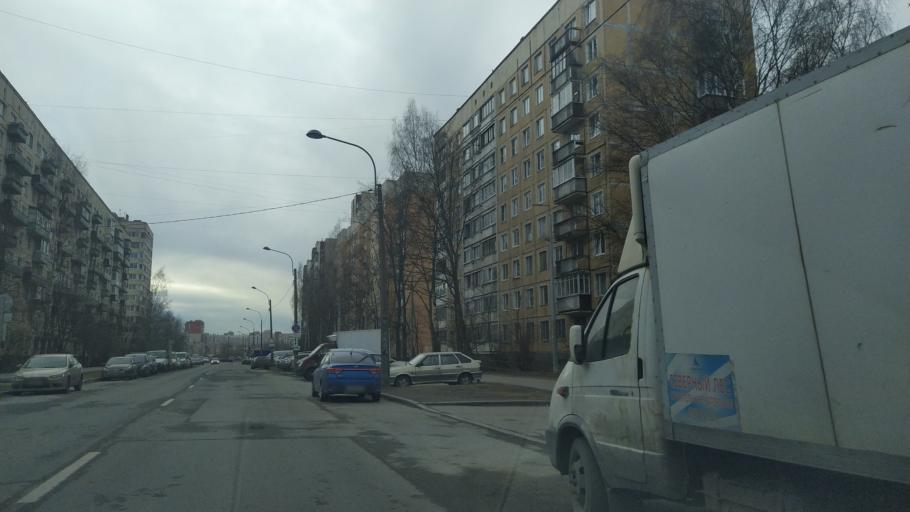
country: RU
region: St.-Petersburg
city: Grazhdanka
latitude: 60.0259
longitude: 30.4222
